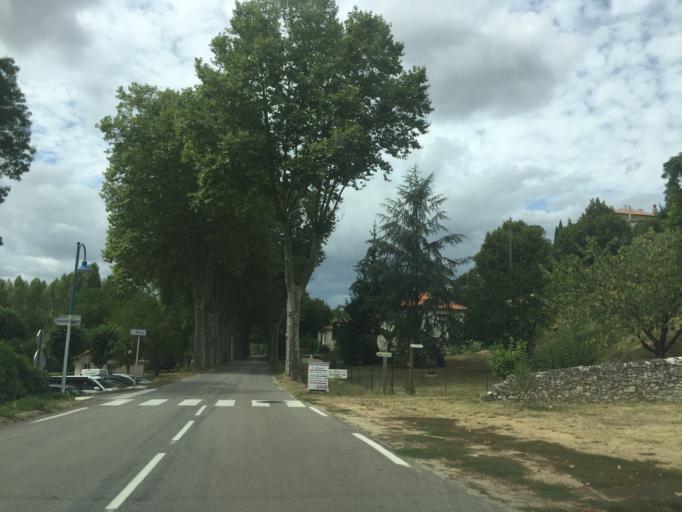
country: FR
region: Midi-Pyrenees
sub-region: Departement du Gers
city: Valence-sur-Baise
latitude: 43.8804
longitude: 0.3809
